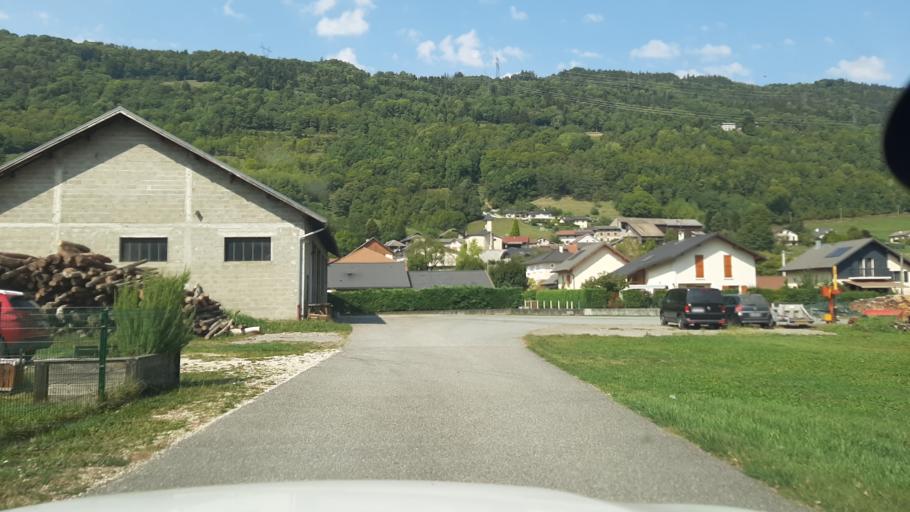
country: FR
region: Rhone-Alpes
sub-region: Departement de la Savoie
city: La Rochette
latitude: 45.4679
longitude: 6.1205
